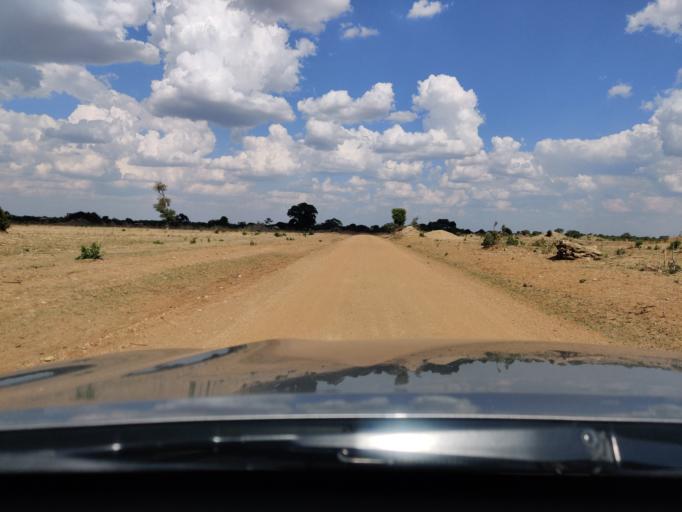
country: ZM
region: Central
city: Chibombo
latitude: -14.7593
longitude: 27.8816
